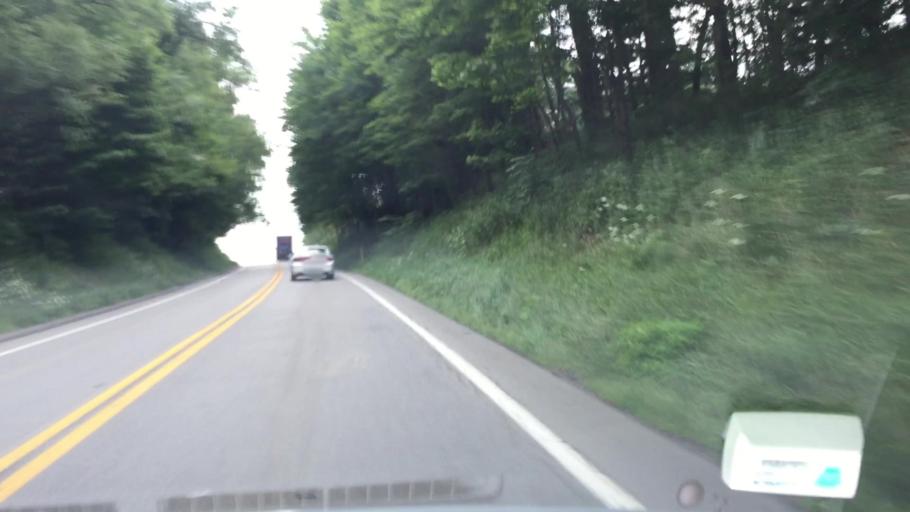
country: US
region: Pennsylvania
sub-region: Butler County
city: Nixon
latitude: 40.7241
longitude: -79.9146
